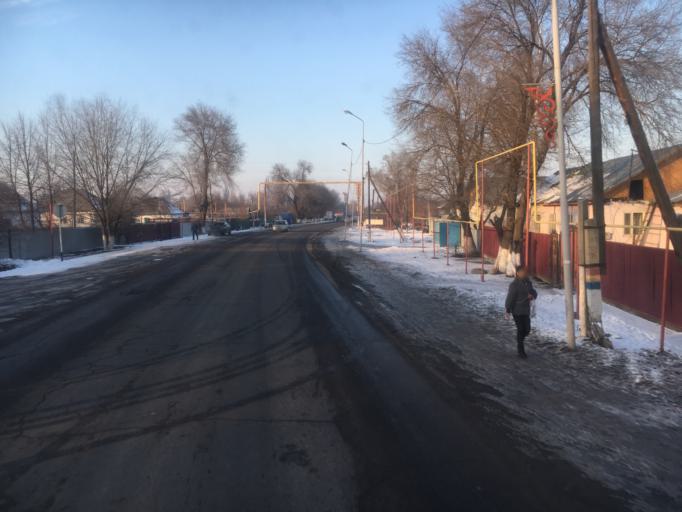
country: KZ
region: Almaty Oblysy
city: Burunday
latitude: 43.3667
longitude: 76.6414
